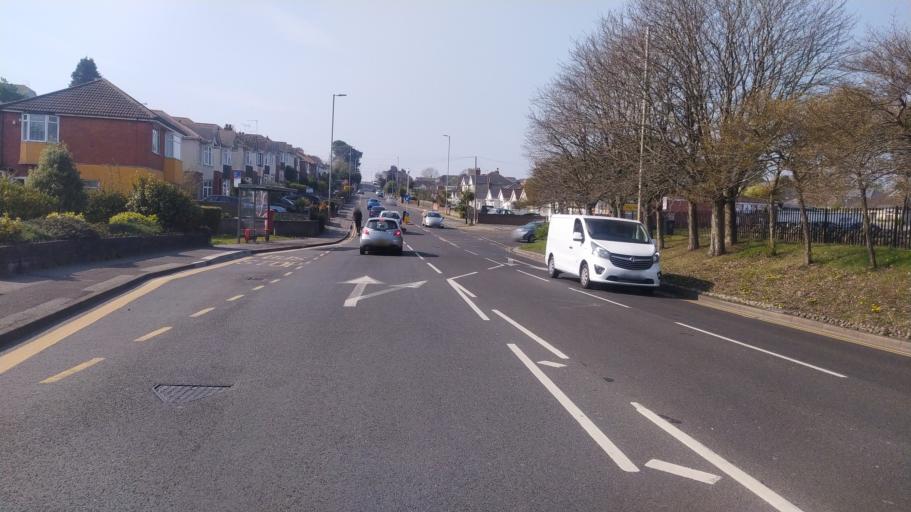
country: GB
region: England
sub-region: Dorset
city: Parkstone
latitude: 50.7321
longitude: -1.9222
